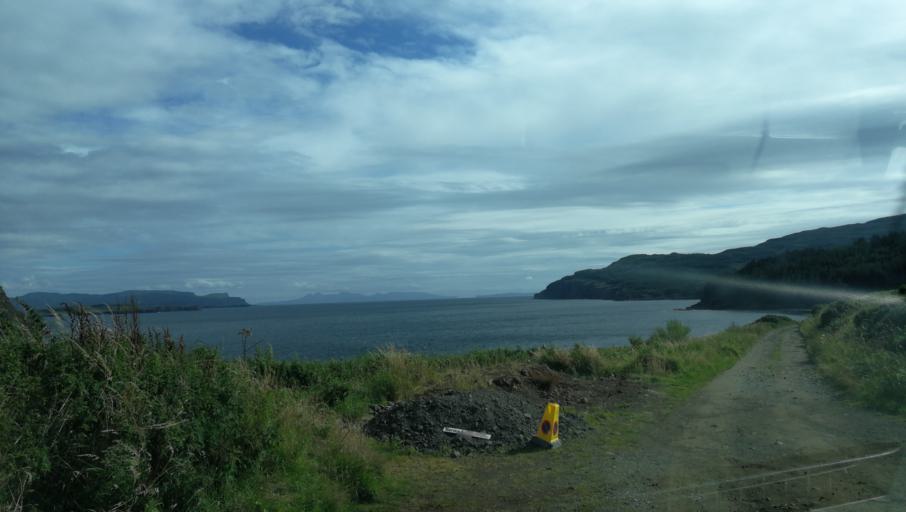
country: GB
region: Scotland
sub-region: Highland
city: Isle of Skye
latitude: 57.3927
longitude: -6.5651
